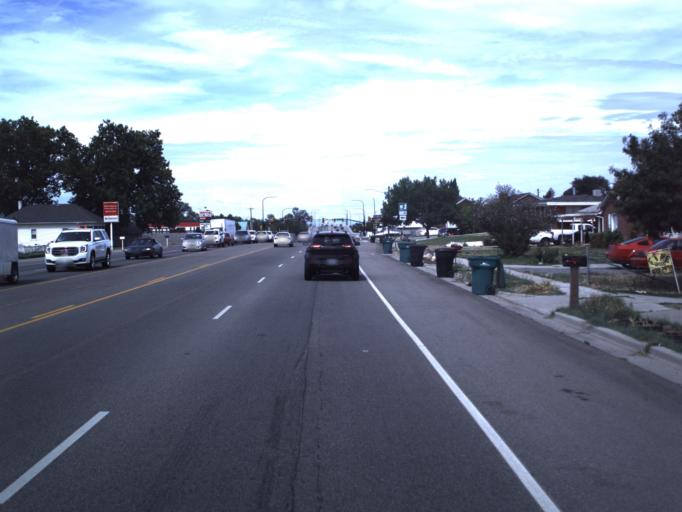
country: US
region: Utah
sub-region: Davis County
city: Clearfield
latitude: 41.1036
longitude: -112.0120
